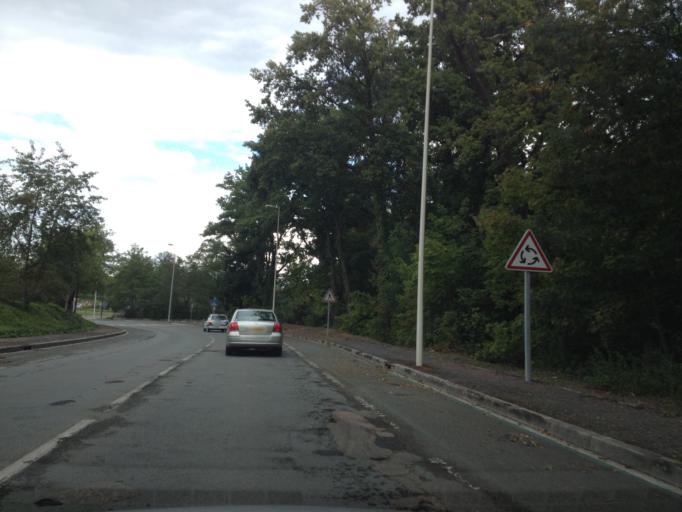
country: FR
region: Rhone-Alpes
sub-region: Departement de la Loire
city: Riorges
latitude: 46.0293
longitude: 4.0474
